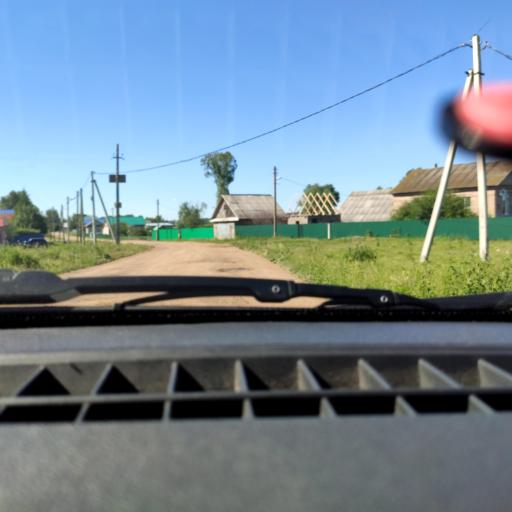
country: RU
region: Bashkortostan
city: Iglino
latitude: 54.8932
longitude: 56.4979
